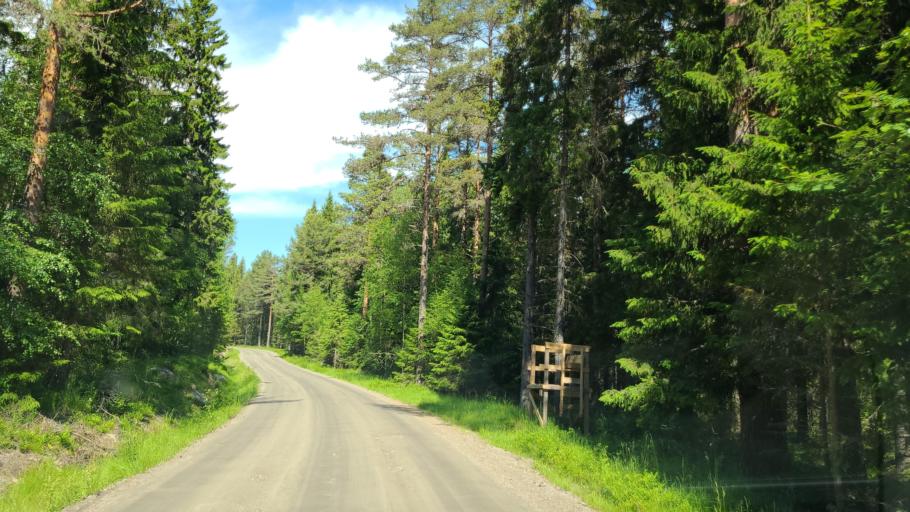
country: SE
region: Vaesterbotten
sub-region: Robertsfors Kommun
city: Robertsfors
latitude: 64.1472
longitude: 20.9564
